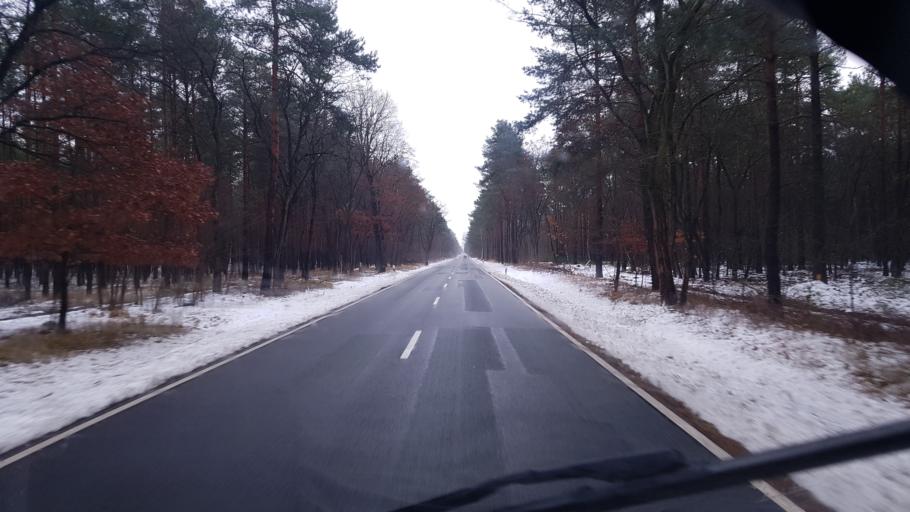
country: DE
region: Brandenburg
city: Tauer
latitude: 51.9819
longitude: 14.4544
